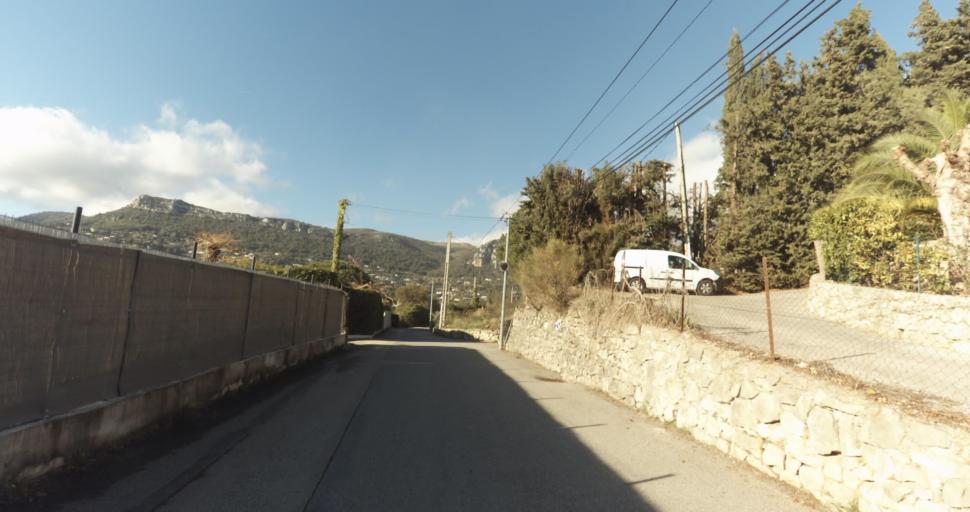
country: FR
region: Provence-Alpes-Cote d'Azur
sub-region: Departement des Alpes-Maritimes
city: La Gaude
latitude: 43.7239
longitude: 7.1337
